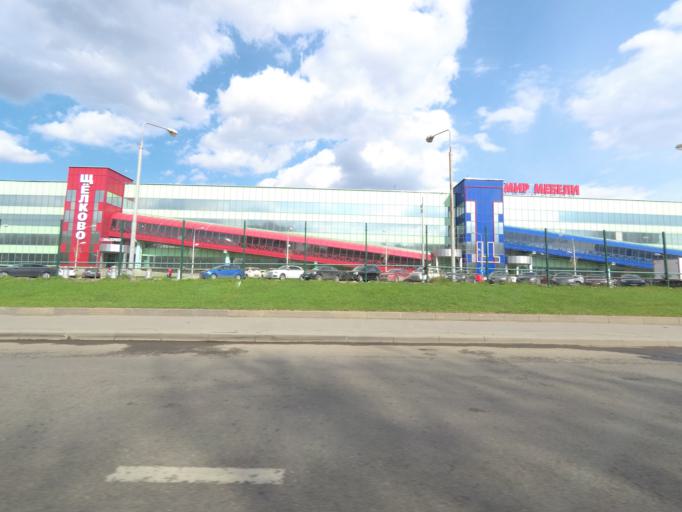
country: RU
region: Moscow
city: Gol'yanovo
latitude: 55.8057
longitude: 37.8301
